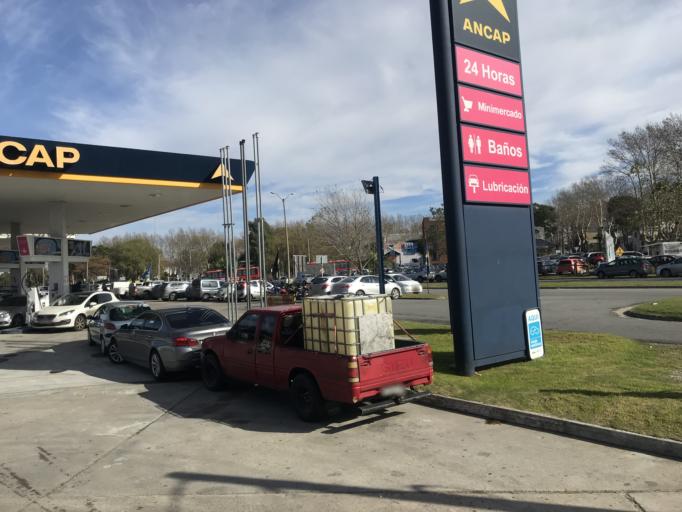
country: UY
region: Colonia
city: Colonia del Sacramento
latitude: -34.4716
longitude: -57.8417
